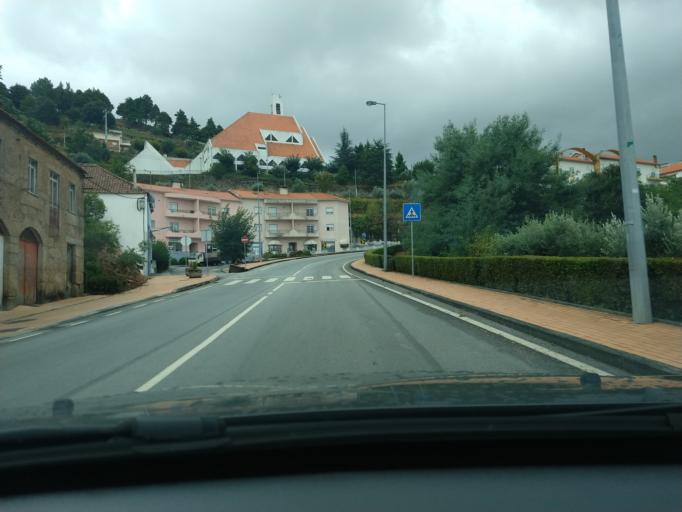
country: PT
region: Guarda
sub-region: Seia
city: Seia
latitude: 40.4032
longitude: -7.7115
